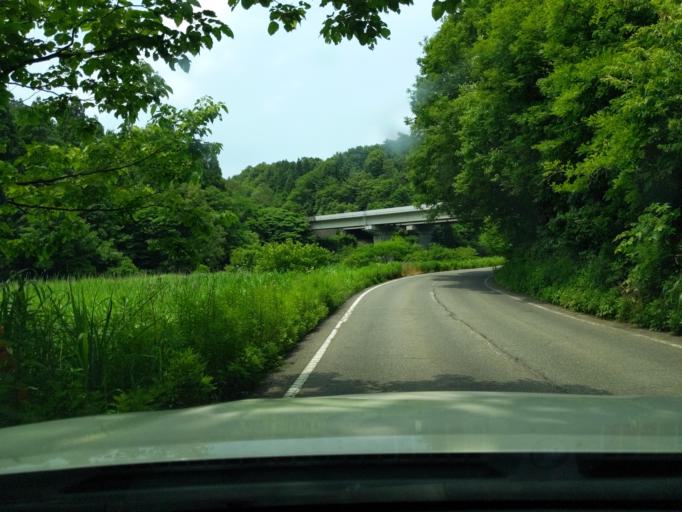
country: JP
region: Niigata
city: Kashiwazaki
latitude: 37.3378
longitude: 138.5543
